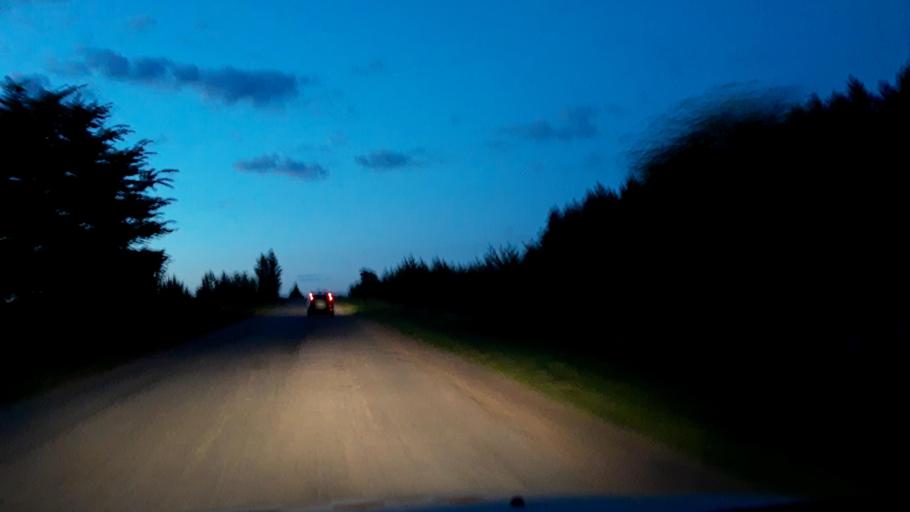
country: RU
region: Nizjnij Novgorod
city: Pamyat' Parizhskoy Kommuny
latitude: 56.0561
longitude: 44.4508
